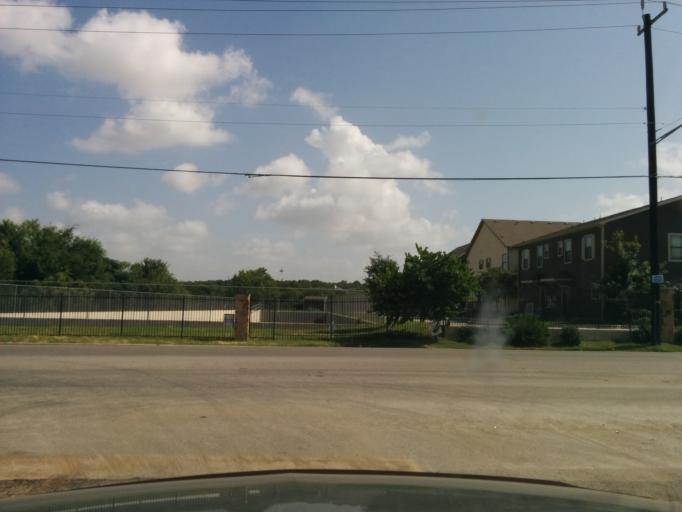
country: US
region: Texas
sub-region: Bexar County
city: Shavano Park
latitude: 29.5723
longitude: -98.6172
